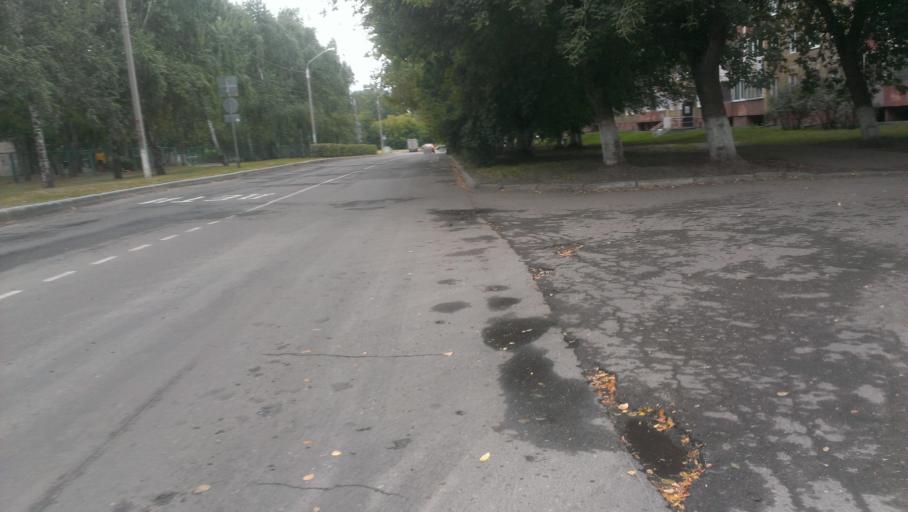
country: RU
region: Altai Krai
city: Novosilikatnyy
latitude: 53.3646
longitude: 83.6679
